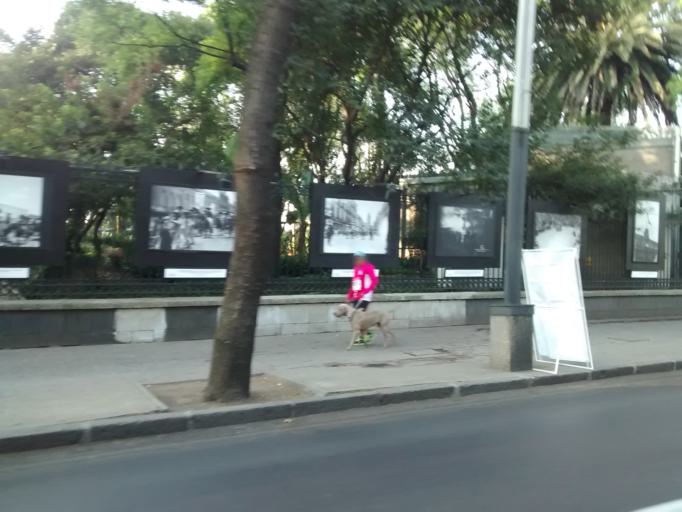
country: MX
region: Mexico City
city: Polanco
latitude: 19.4245
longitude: -99.1843
